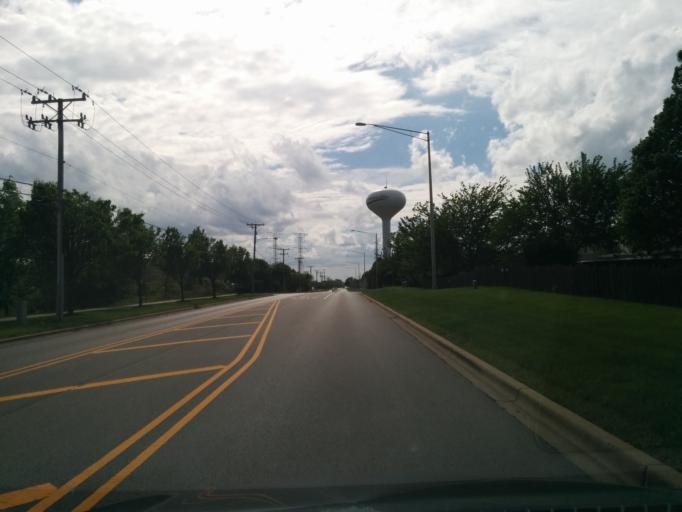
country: US
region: Illinois
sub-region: Will County
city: Romeoville
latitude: 41.6241
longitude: -88.1344
